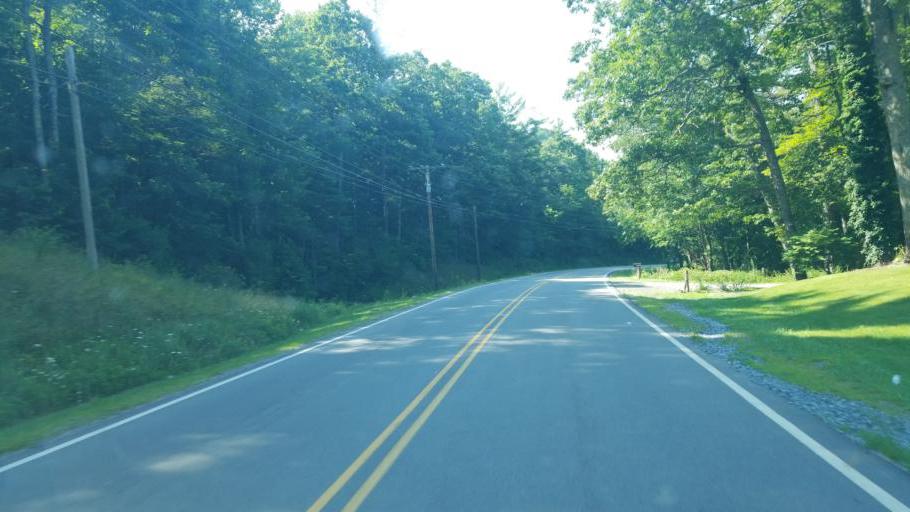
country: US
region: North Carolina
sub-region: Avery County
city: Newland
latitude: 36.0436
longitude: -81.9140
